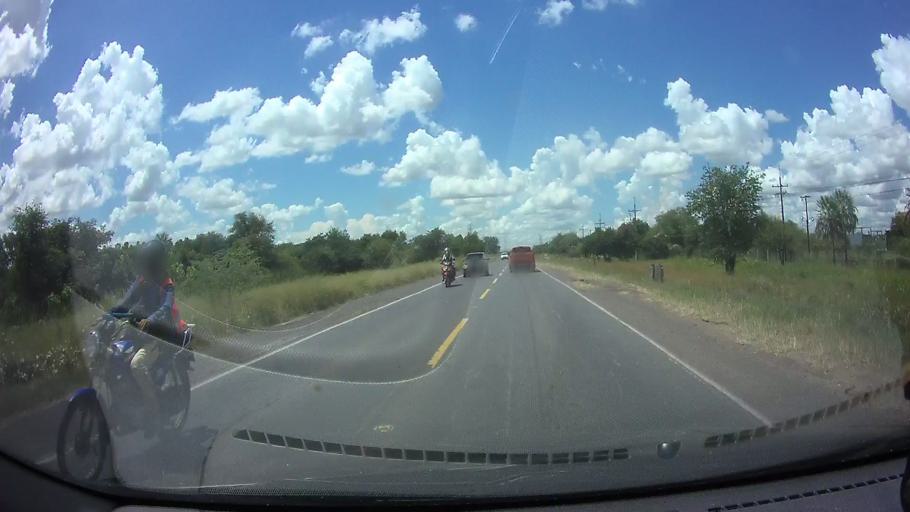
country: PY
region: Central
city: Colonia Mariano Roque Alonso
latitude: -25.1838
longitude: -57.5916
